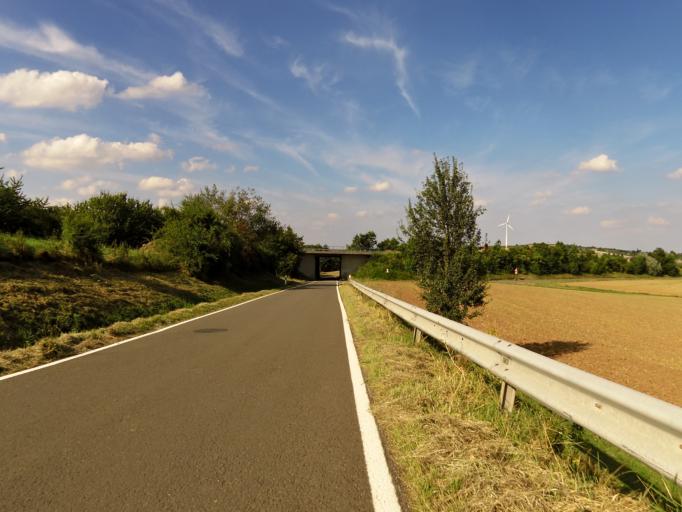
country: DE
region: Rheinland-Pfalz
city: Tiefenthal
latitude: 49.5320
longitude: 8.1014
